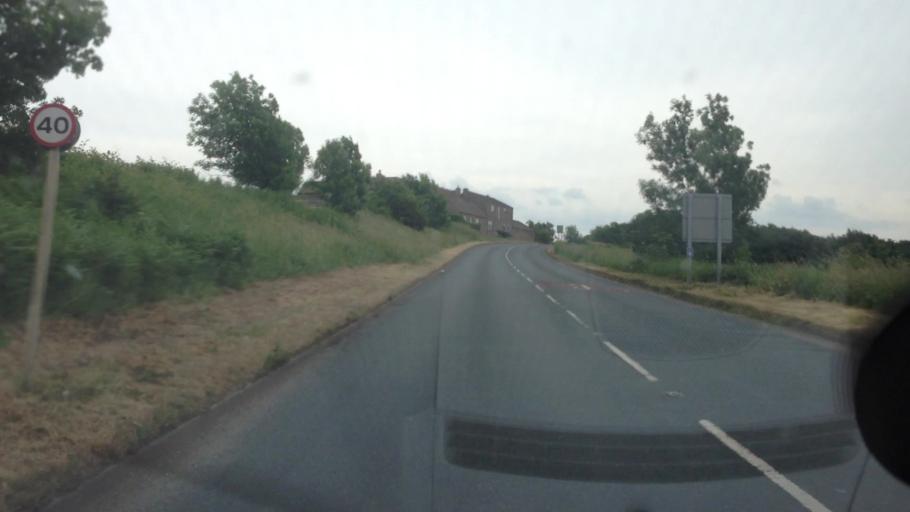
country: GB
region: England
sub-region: City and Borough of Wakefield
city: Woolley
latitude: 53.6143
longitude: -1.5365
